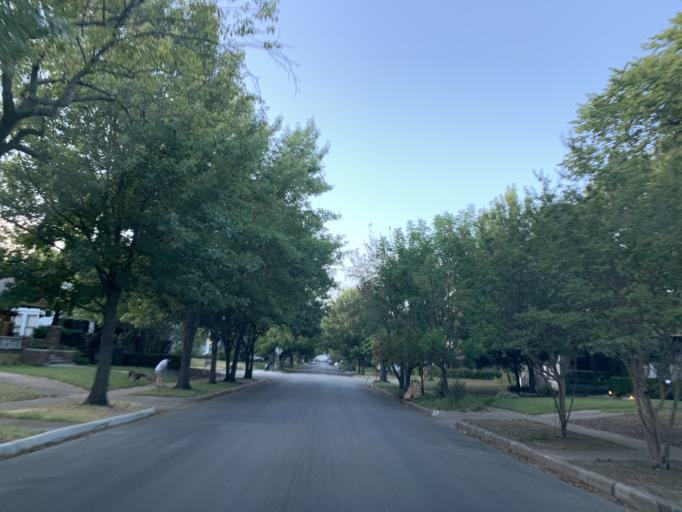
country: US
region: Texas
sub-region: Dallas County
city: Cockrell Hill
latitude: 32.7459
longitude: -96.8404
